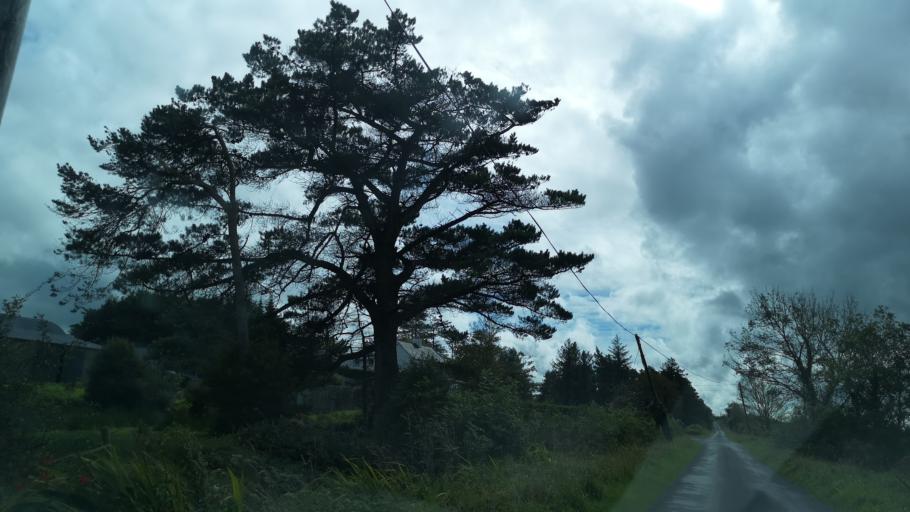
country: IE
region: Connaught
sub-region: County Galway
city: Athenry
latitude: 53.2876
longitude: -8.6653
